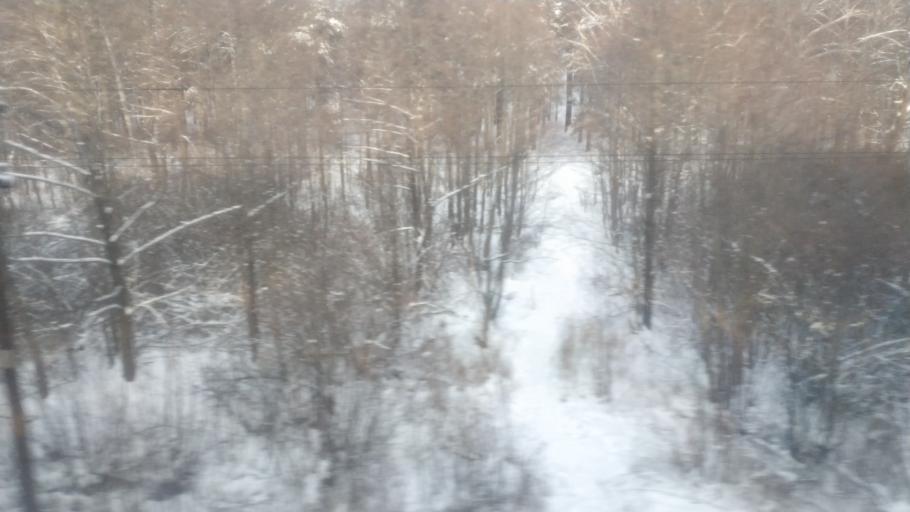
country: RU
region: Kirov
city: Krasnaya Polyana
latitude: 56.2501
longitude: 51.1507
